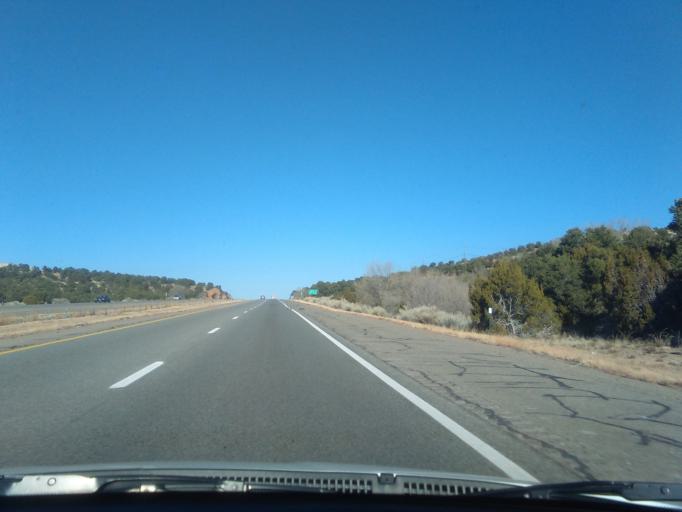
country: US
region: New Mexico
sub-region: Santa Fe County
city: Santa Fe
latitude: 35.6090
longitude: -105.9139
